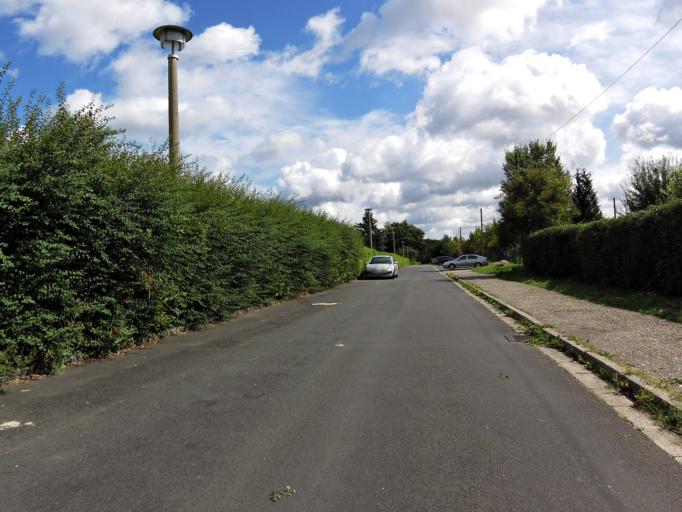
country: DE
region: Saxony
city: Markkleeberg
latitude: 51.3020
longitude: 12.4057
